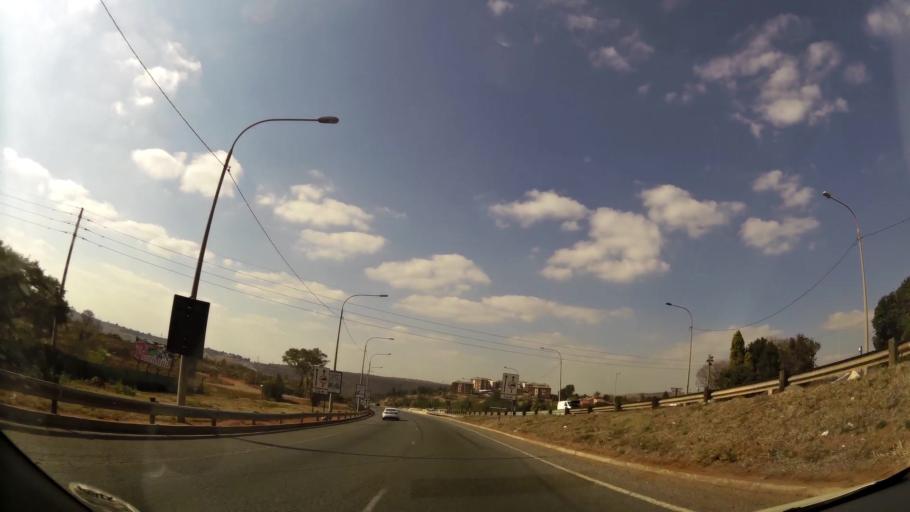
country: ZA
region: Gauteng
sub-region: West Rand District Municipality
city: Krugersdorp
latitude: -26.0770
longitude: 27.7947
